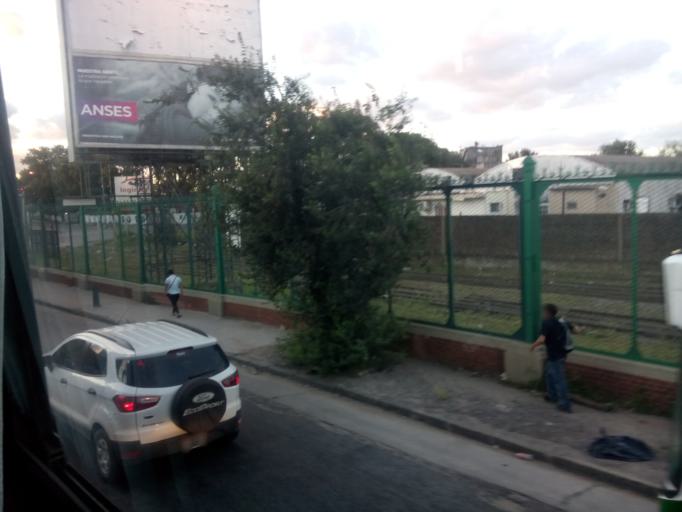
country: AR
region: Buenos Aires F.D.
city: Retiro
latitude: -34.5784
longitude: -58.3848
